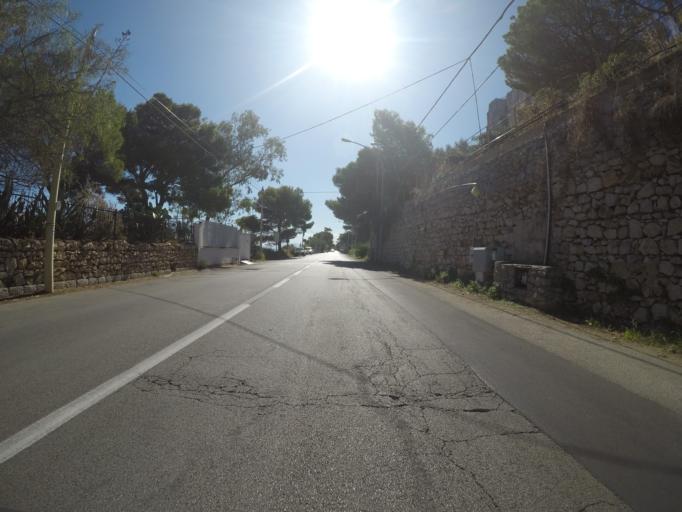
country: IT
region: Sicily
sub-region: Palermo
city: Palermo
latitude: 38.1866
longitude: 13.3608
